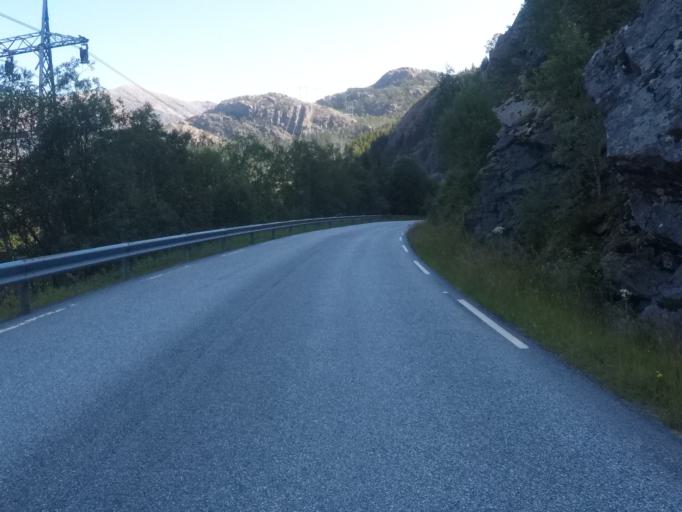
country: NO
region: Sogn og Fjordane
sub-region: Bremanger
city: Svelgen
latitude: 61.7784
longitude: 5.3309
